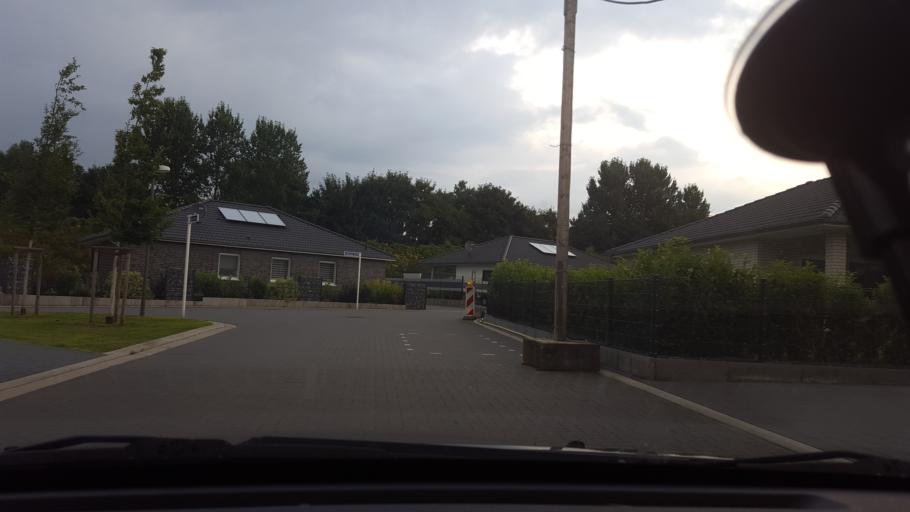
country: DE
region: North Rhine-Westphalia
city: Marl
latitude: 51.6545
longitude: 7.1403
